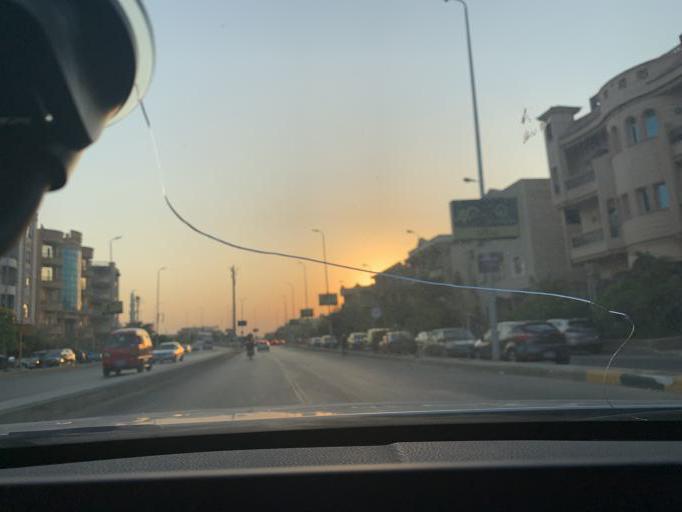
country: EG
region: Muhafazat al Qahirah
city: Cairo
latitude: 30.0059
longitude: 31.4488
